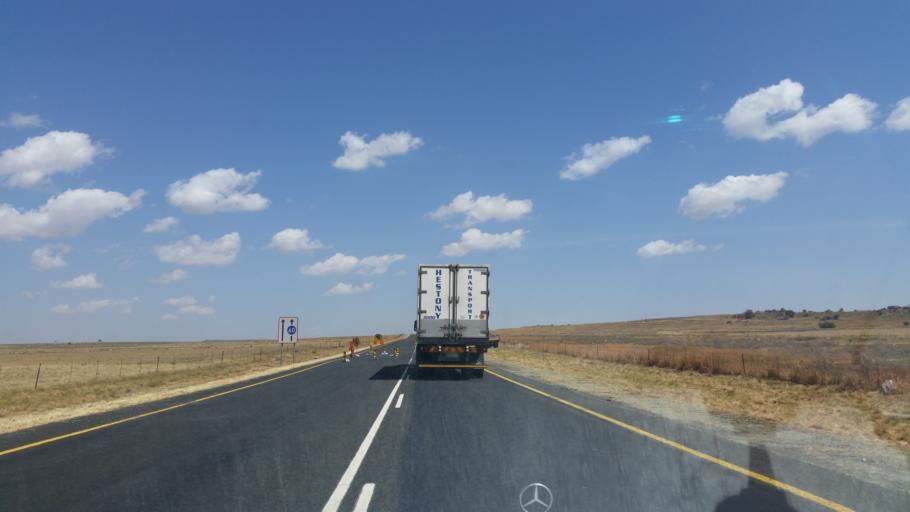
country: ZA
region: Orange Free State
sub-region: Thabo Mofutsanyana District Municipality
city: Senekal
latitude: -28.3103
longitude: 27.8459
